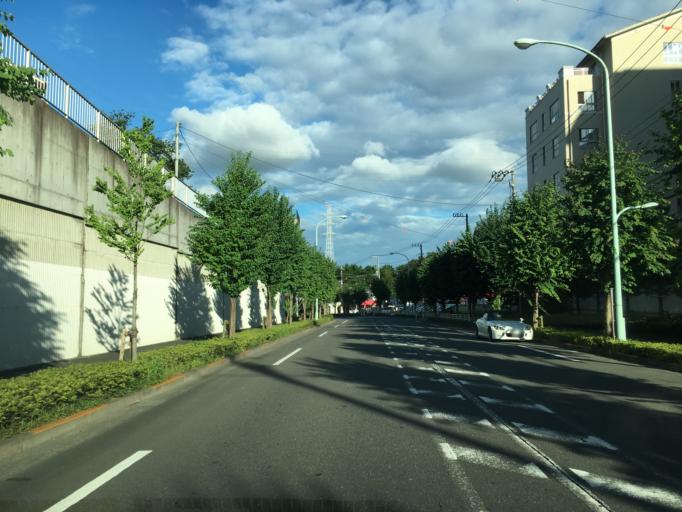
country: JP
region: Tokyo
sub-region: Machida-shi
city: Machida
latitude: 35.5949
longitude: 139.4464
